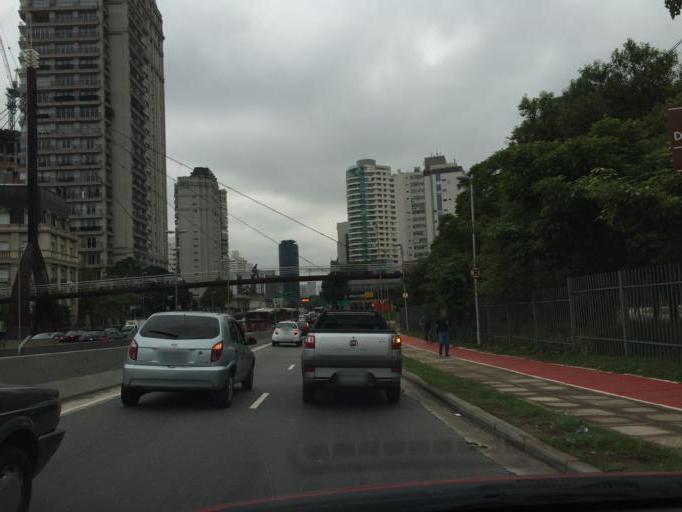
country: BR
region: Sao Paulo
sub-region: Sao Paulo
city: Sao Paulo
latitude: -23.5865
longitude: -46.6896
